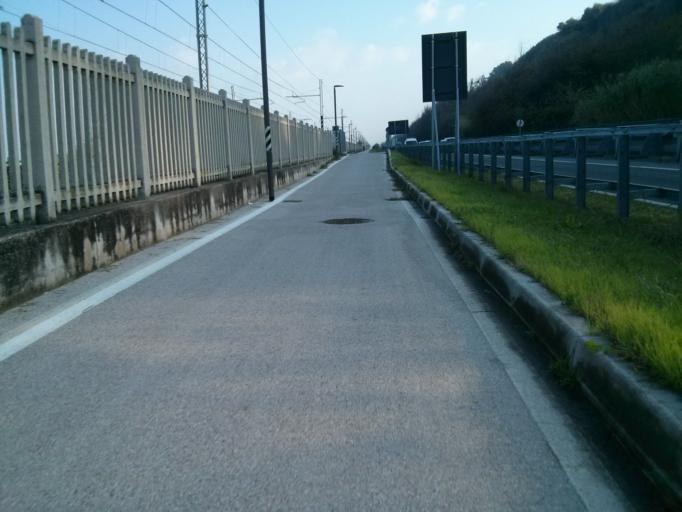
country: IT
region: The Marches
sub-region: Provincia di Pesaro e Urbino
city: Fenile
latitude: 43.8783
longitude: 12.9657
